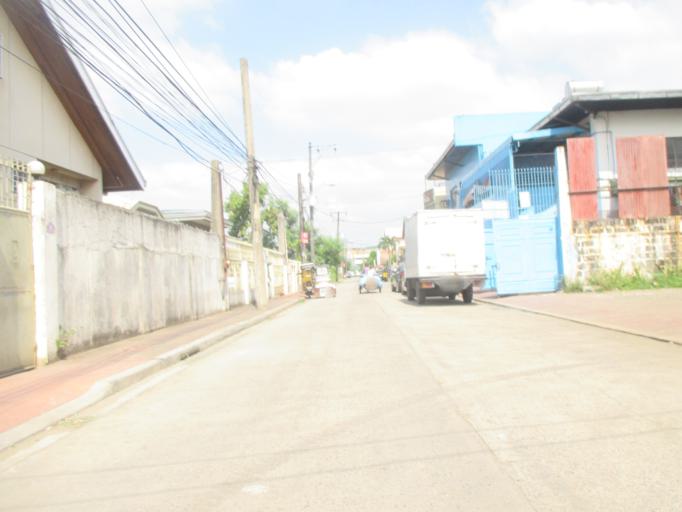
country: PH
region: Metro Manila
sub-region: Marikina
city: Calumpang
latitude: 14.6304
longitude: 121.1005
